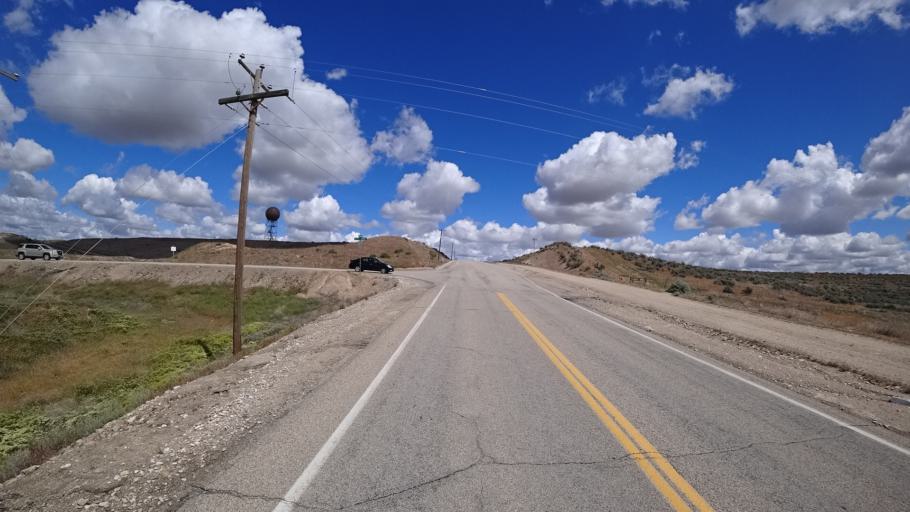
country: US
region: Idaho
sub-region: Ada County
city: Boise
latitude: 43.4879
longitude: -116.2340
